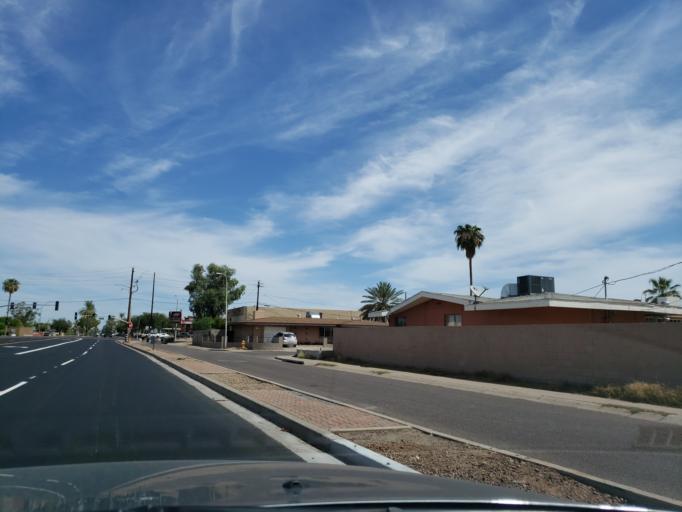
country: US
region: Arizona
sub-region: Maricopa County
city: Glendale
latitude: 33.5083
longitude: -112.1863
